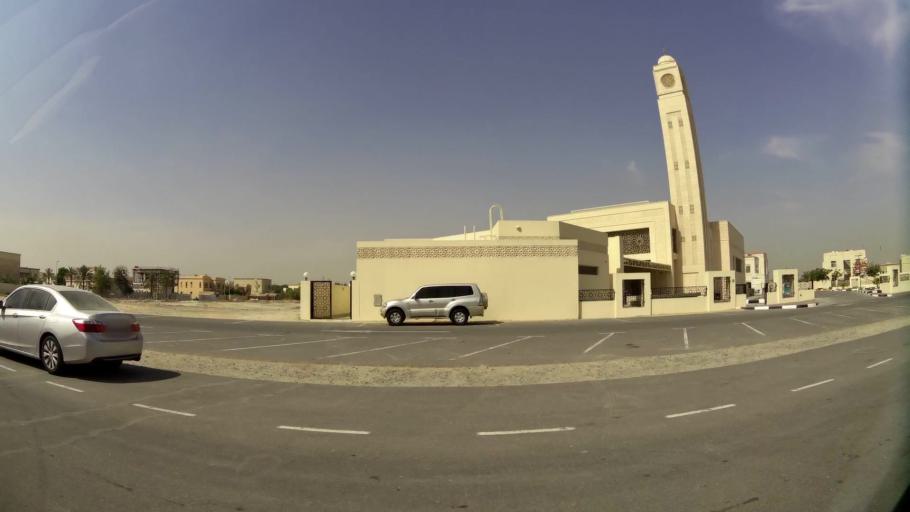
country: AE
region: Ash Shariqah
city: Sharjah
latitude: 25.2743
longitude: 55.3979
